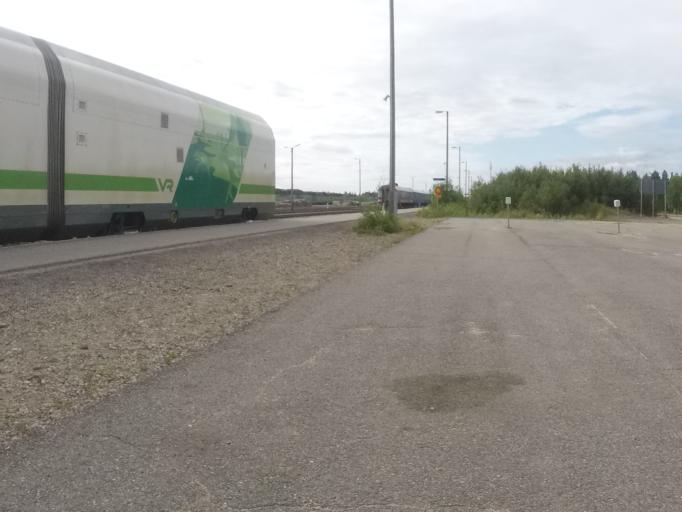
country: FI
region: Lapland
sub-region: Tunturi-Lappi
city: Kolari
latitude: 67.3522
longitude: 23.8361
